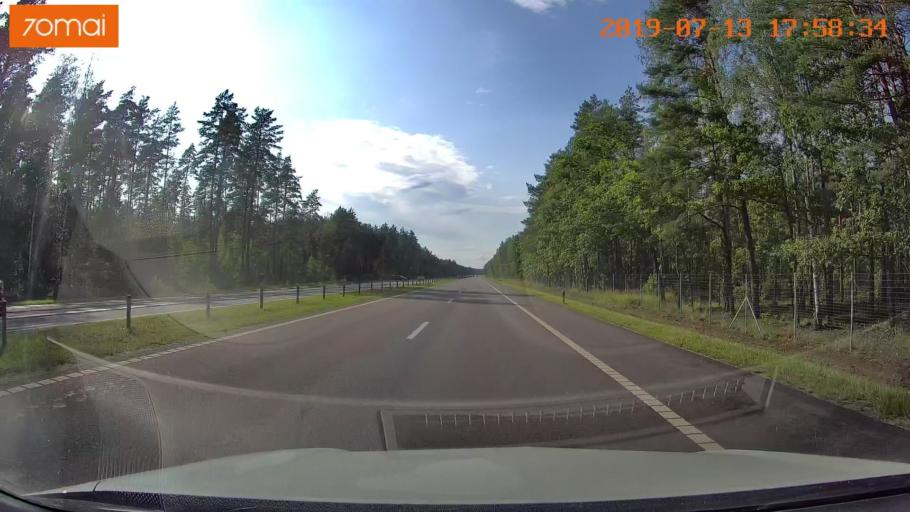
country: BY
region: Minsk
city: Pukhavichy
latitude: 53.4672
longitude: 28.3903
